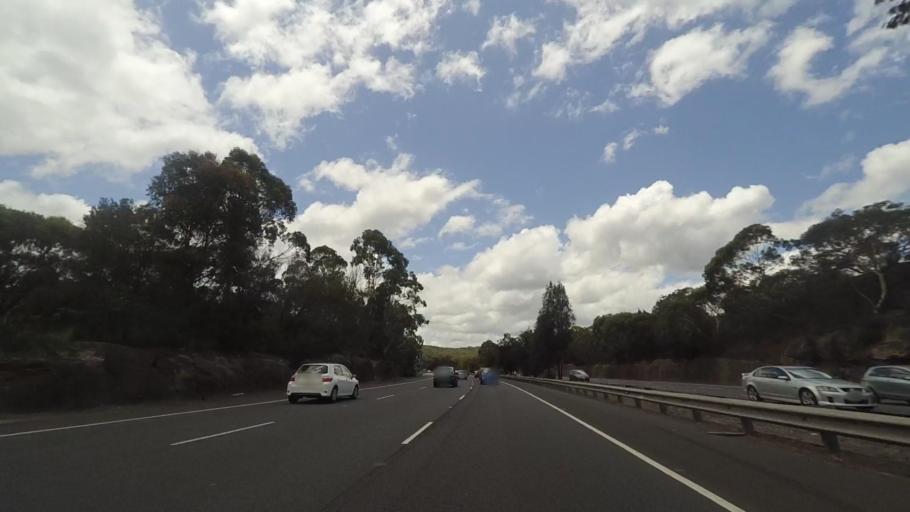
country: AU
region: New South Wales
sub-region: Ku-ring-gai
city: North Wahroonga
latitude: -33.6960
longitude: 151.1205
